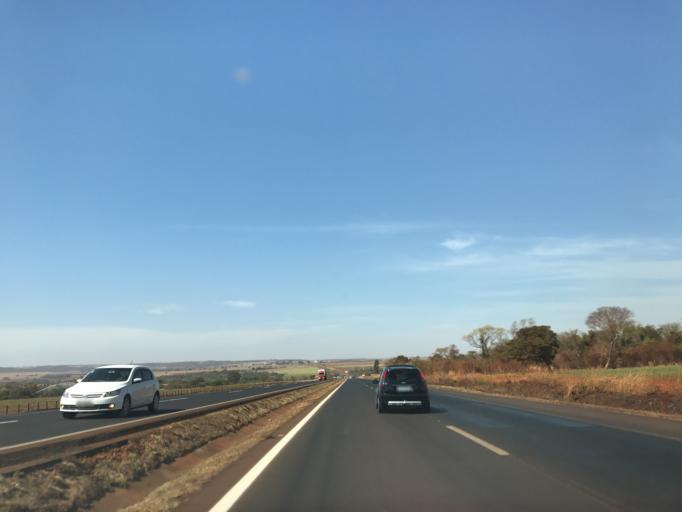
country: BR
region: Minas Gerais
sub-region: Centralina
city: Centralina
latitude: -18.5233
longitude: -49.1908
